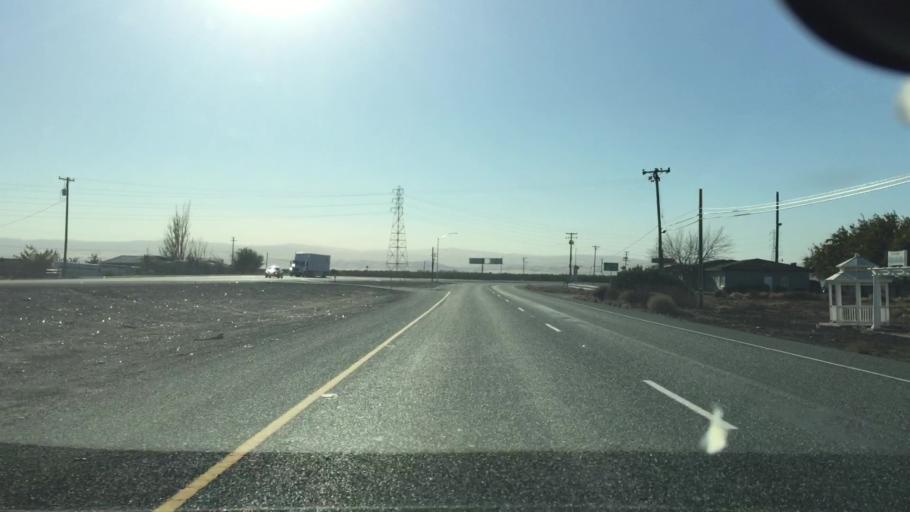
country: US
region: California
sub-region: San Joaquin County
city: Tracy
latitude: 37.7417
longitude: -121.3675
